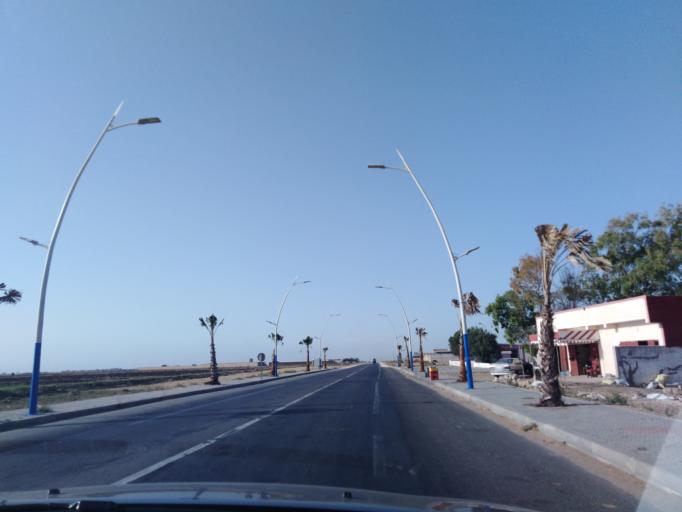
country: MA
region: Doukkala-Abda
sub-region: El-Jadida
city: Sidi Bennour
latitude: 32.5882
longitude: -8.7101
